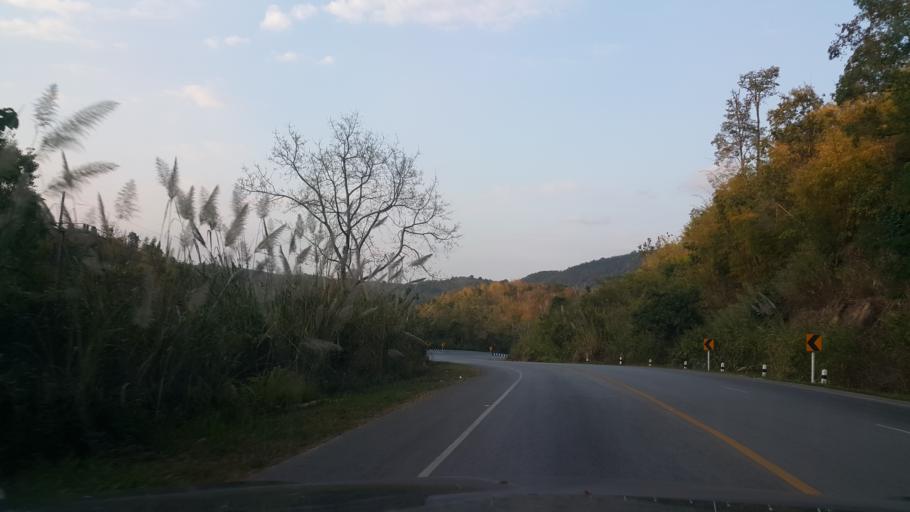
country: TH
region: Loei
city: Phu Ruea
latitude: 17.4733
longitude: 101.5385
